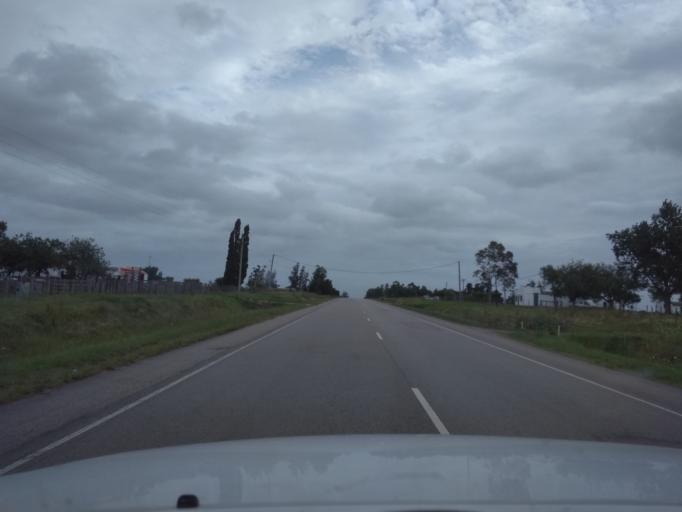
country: UY
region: Canelones
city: Tala
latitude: -34.3171
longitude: -55.7444
